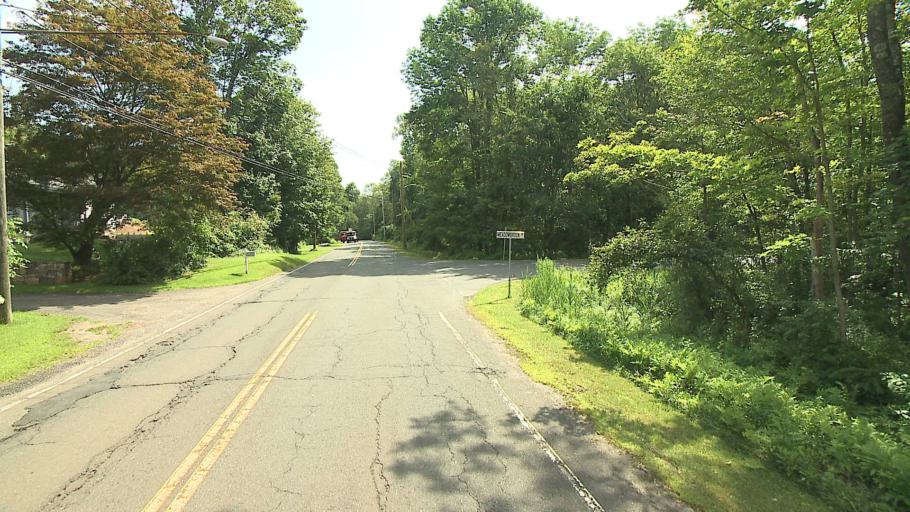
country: US
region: New York
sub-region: Putnam County
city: Putnam Lake
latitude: 41.4706
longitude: -73.5105
